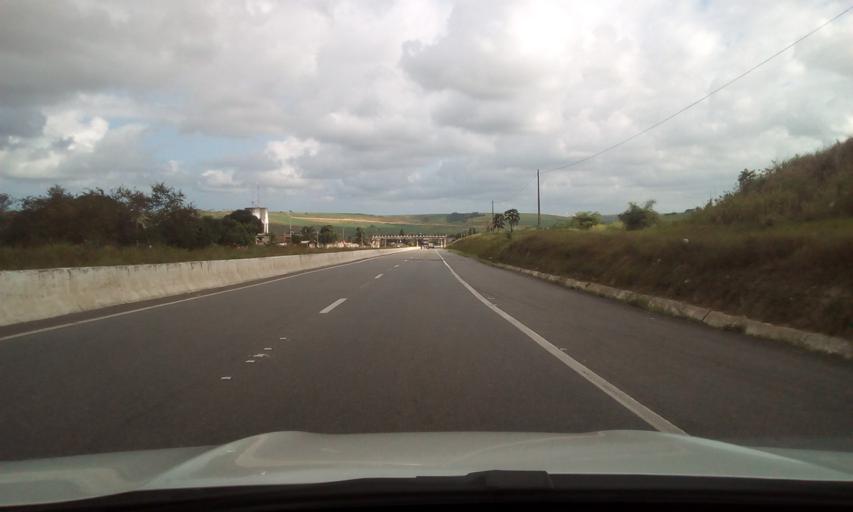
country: BR
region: Pernambuco
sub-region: Itapissuma
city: Itapissuma
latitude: -7.7448
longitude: -34.9387
